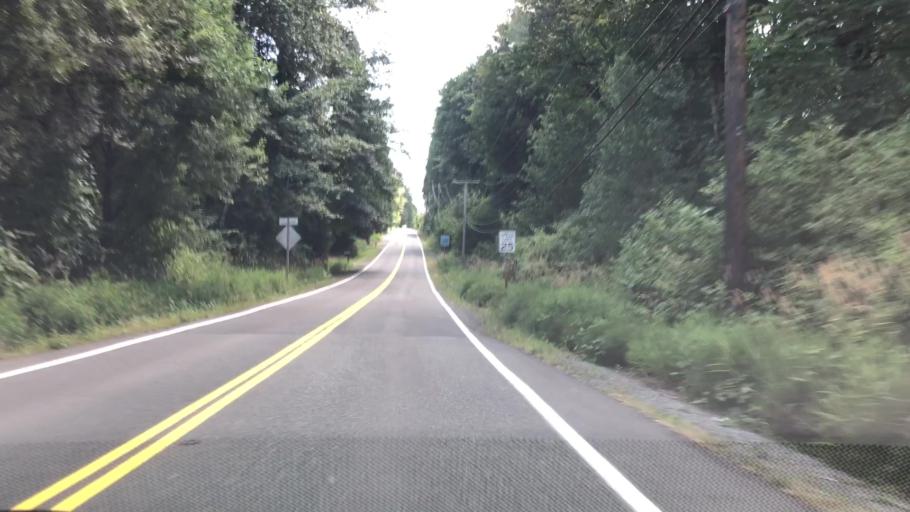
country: US
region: Washington
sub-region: King County
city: Cottage Lake
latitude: 47.7521
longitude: -122.0535
